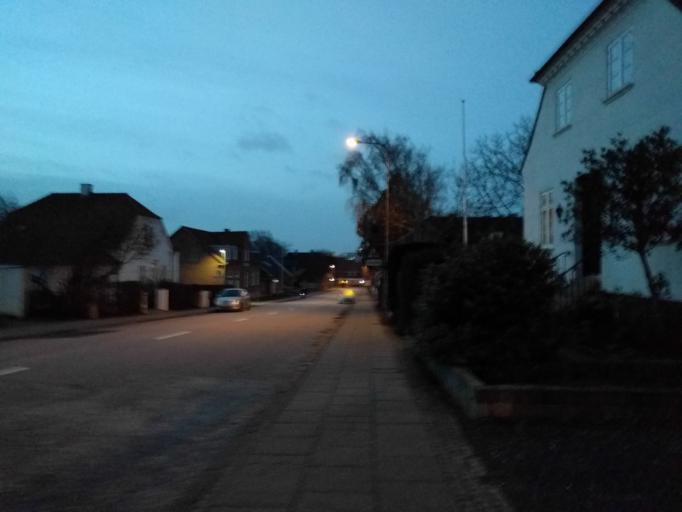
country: DK
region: North Denmark
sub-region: Alborg Kommune
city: Aalborg
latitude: 57.0616
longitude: 9.9237
